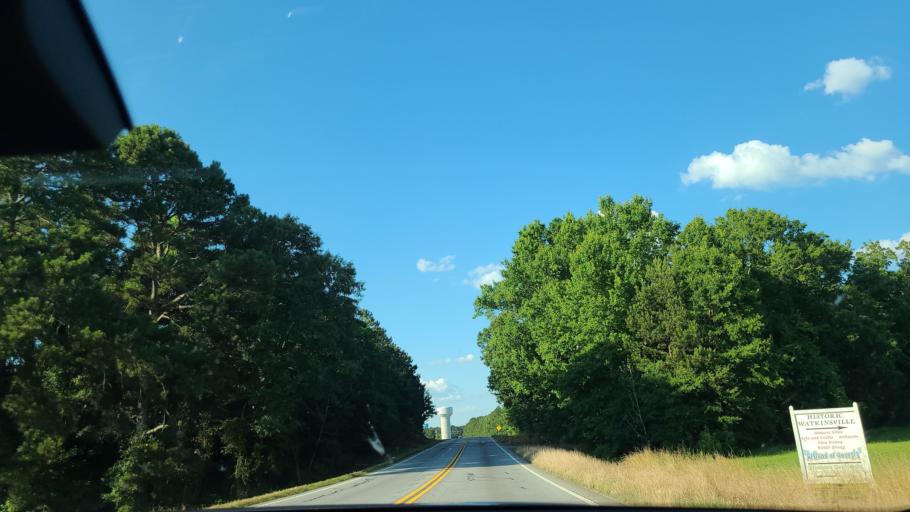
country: US
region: Georgia
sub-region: Oconee County
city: Watkinsville
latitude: 33.8399
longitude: -83.4269
